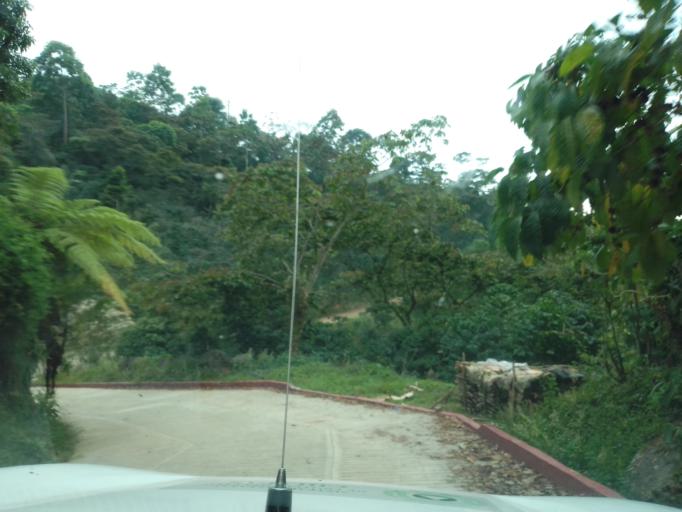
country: MX
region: Chiapas
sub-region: Union Juarez
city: Santo Domingo
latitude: 15.0670
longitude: -92.1163
